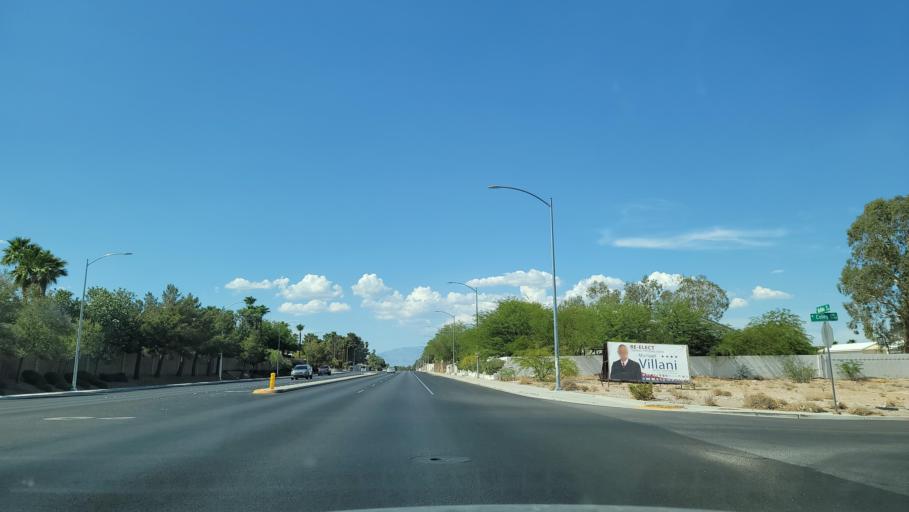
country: US
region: Nevada
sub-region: Clark County
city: Spring Valley
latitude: 36.1344
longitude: -115.2609
